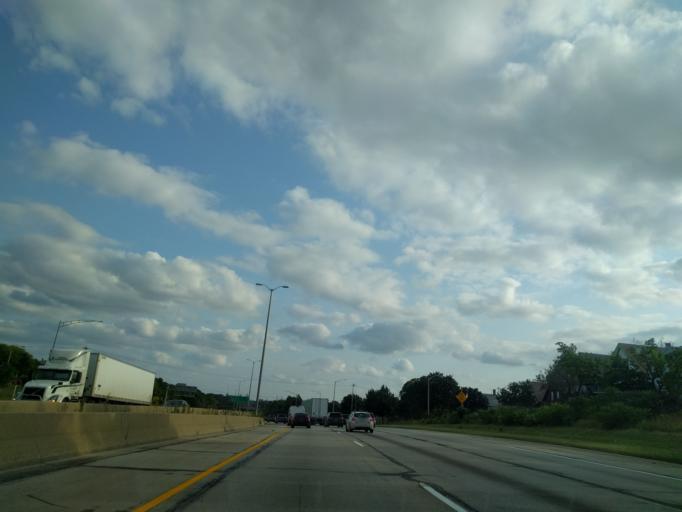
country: US
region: Wisconsin
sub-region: Milwaukee County
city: Shorewood
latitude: 43.0804
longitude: -87.9207
